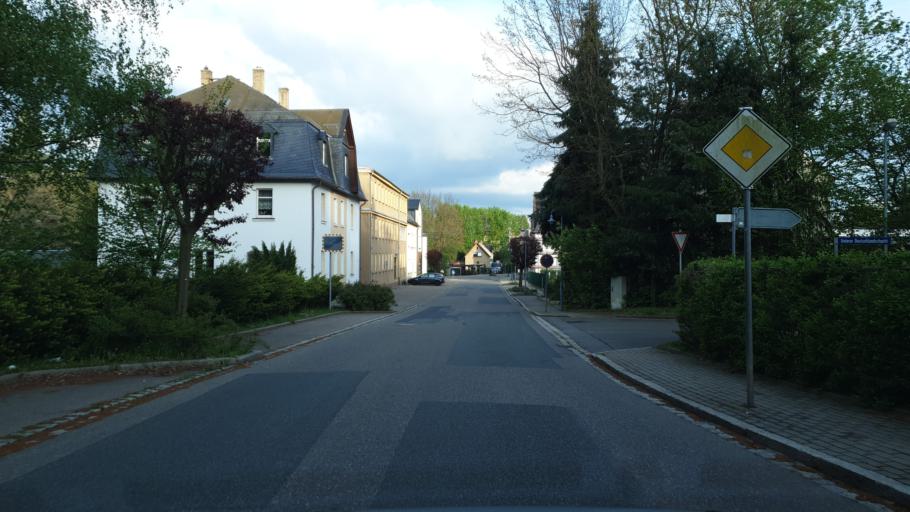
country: DE
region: Saxony
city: Oelsnitz
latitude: 50.7293
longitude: 12.6954
